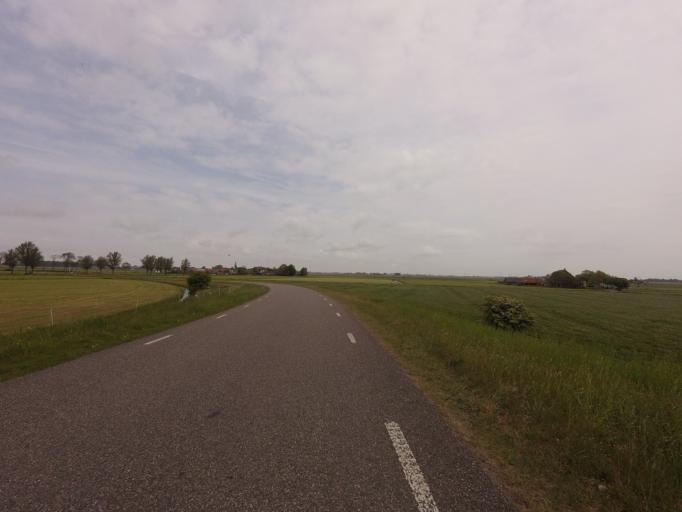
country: NL
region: Friesland
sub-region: Sudwest Fryslan
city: Bolsward
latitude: 53.0766
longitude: 5.4804
